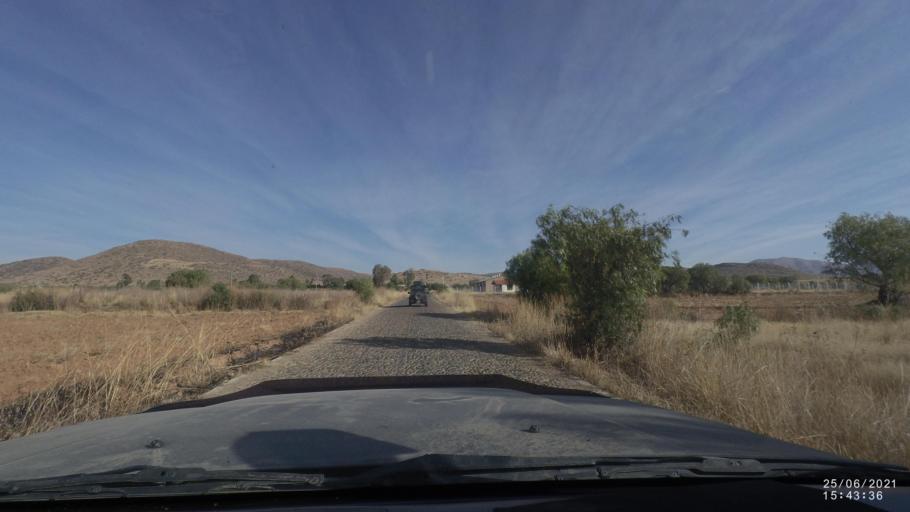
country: BO
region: Cochabamba
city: Cliza
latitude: -17.6499
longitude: -65.9126
